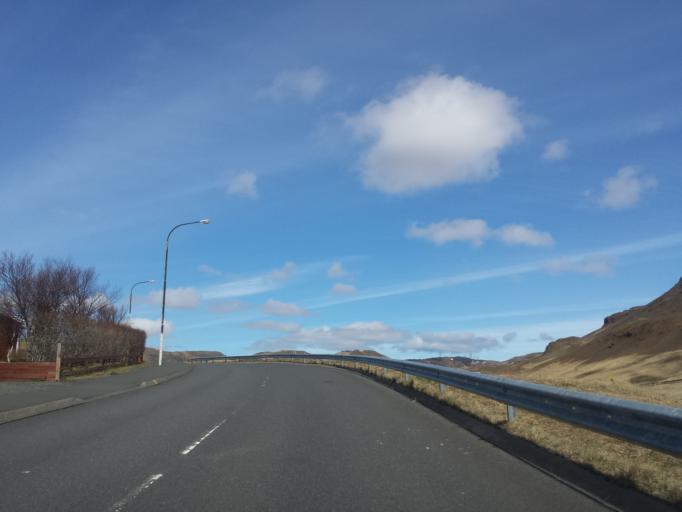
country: IS
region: South
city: Hveragerdi
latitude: 64.0047
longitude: -21.1848
